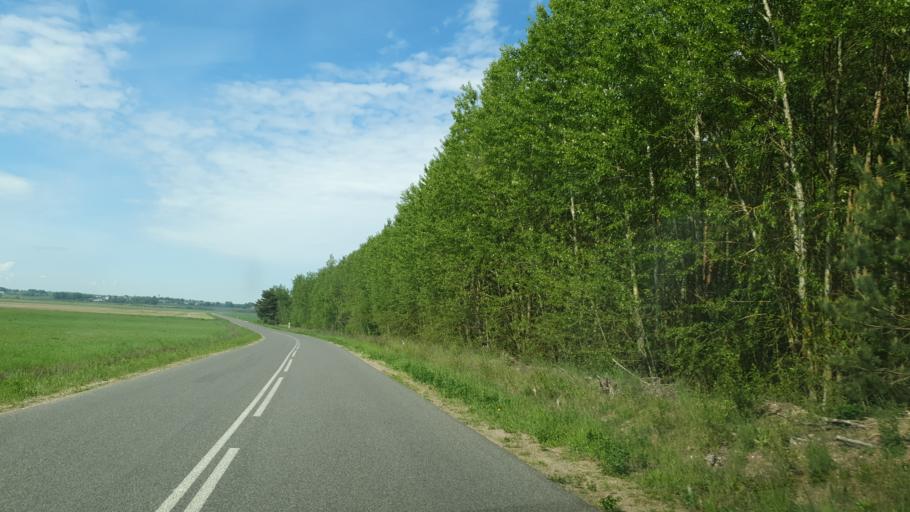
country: BY
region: Grodnenskaya
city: Mir
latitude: 53.4228
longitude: 26.3622
